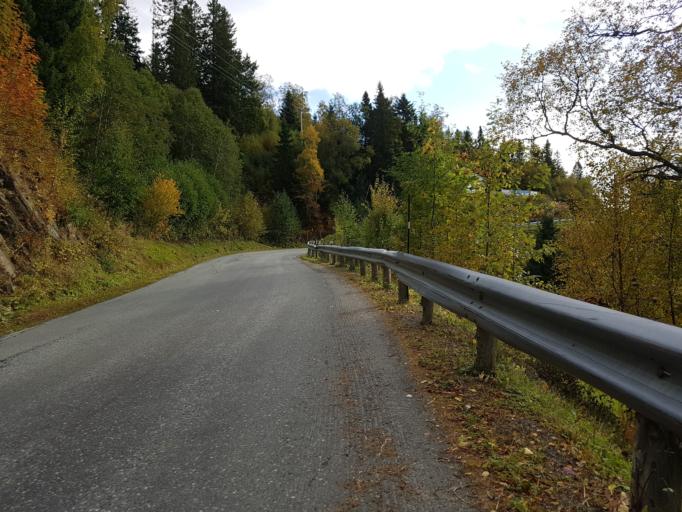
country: NO
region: Sor-Trondelag
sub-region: Klaebu
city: Klaebu
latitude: 63.3928
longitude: 10.5562
